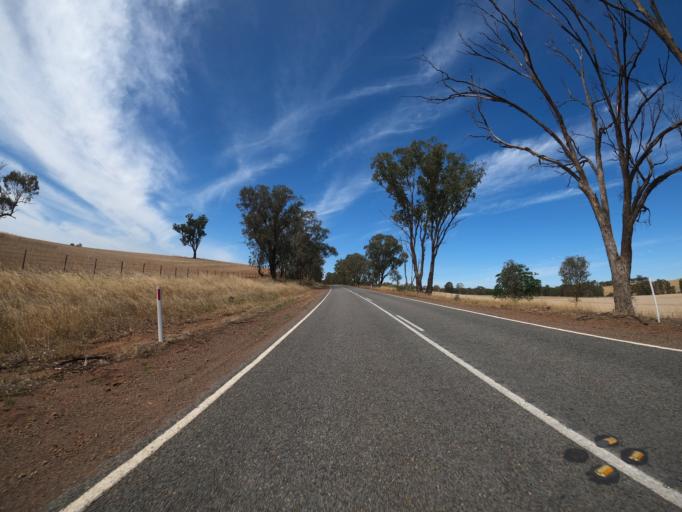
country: AU
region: Victoria
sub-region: Benalla
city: Benalla
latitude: -36.3360
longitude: 145.9591
